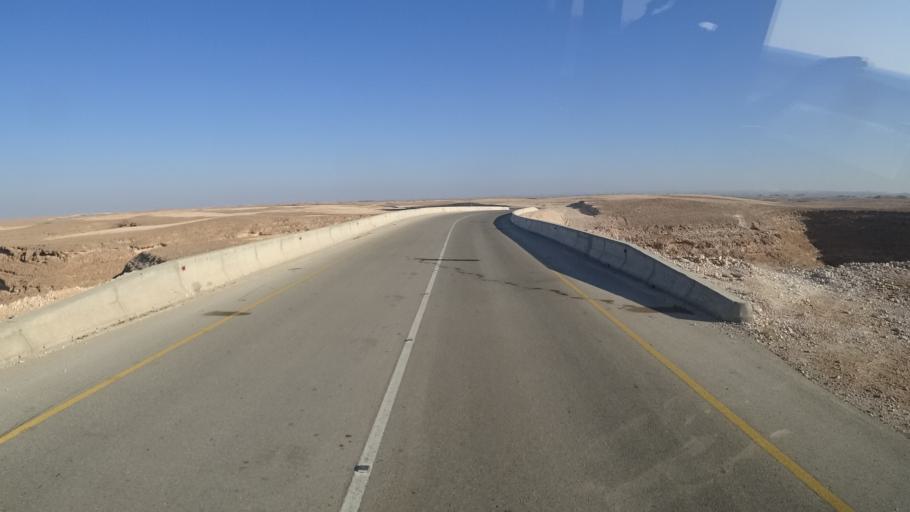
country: YE
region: Al Mahrah
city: Hawf
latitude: 17.0824
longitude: 53.0120
